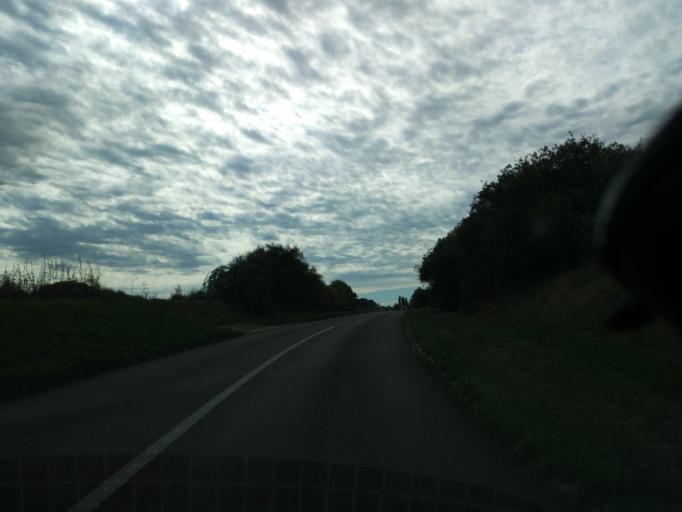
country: FR
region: Ile-de-France
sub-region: Departement de l'Essonne
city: Les Molieres
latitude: 48.6814
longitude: 2.0754
